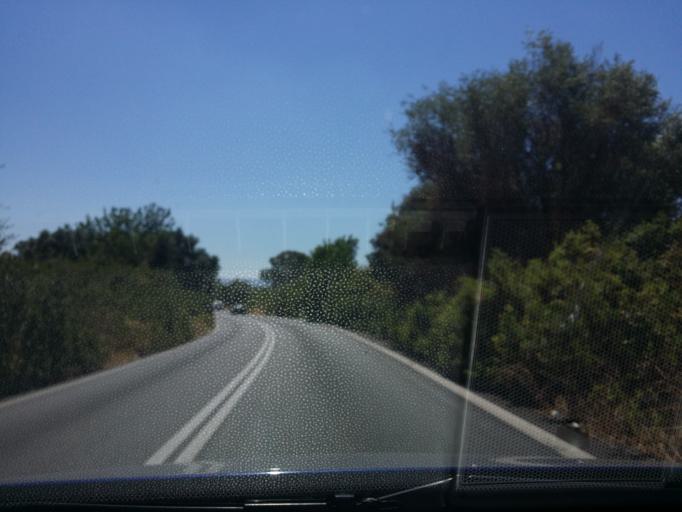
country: GR
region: Peloponnese
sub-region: Nomos Lakonias
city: Skala
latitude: 36.8448
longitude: 22.6409
